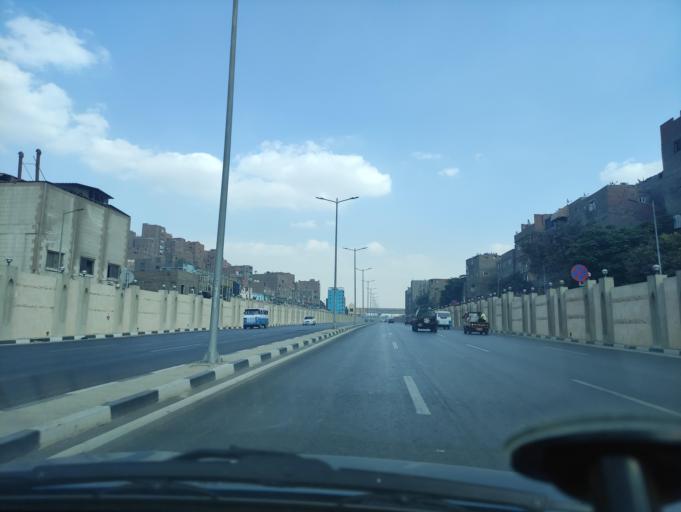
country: EG
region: Muhafazat al Qahirah
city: Cairo
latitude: 30.0451
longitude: 31.2913
